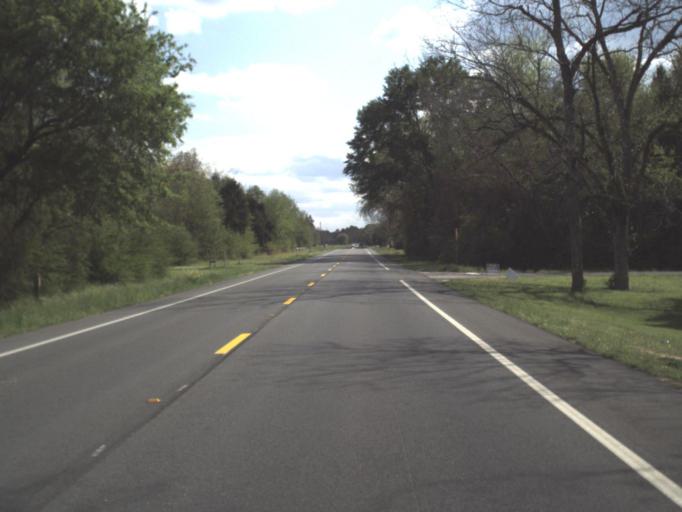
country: US
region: Florida
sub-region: Okaloosa County
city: Crestview
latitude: 30.9134
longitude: -86.4869
